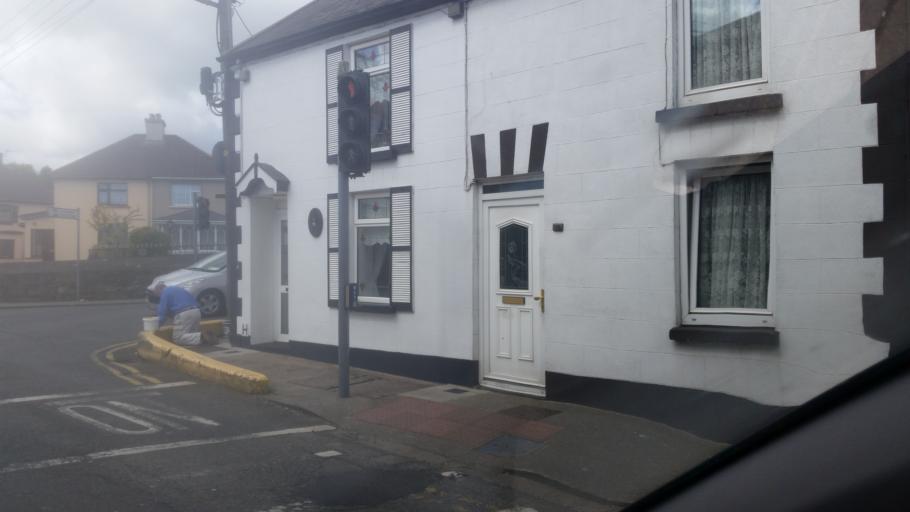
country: IE
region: Leinster
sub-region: Loch Garman
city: Loch Garman
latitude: 52.3332
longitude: -6.4607
